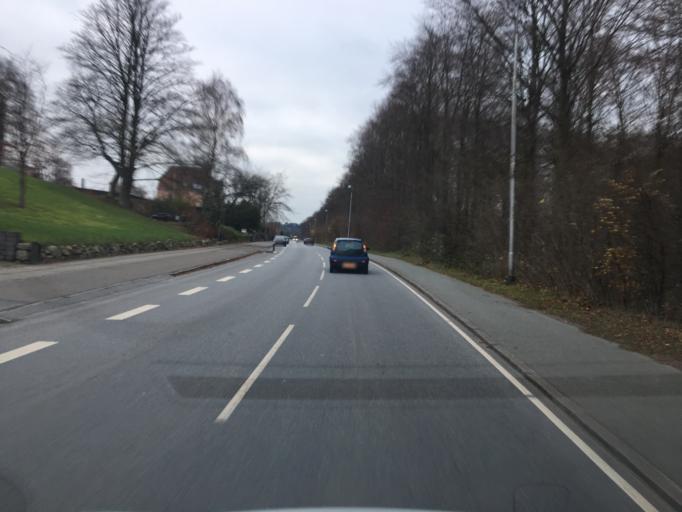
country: DK
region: South Denmark
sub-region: Aabenraa Kommune
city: Aabenraa
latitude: 55.0343
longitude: 9.3990
